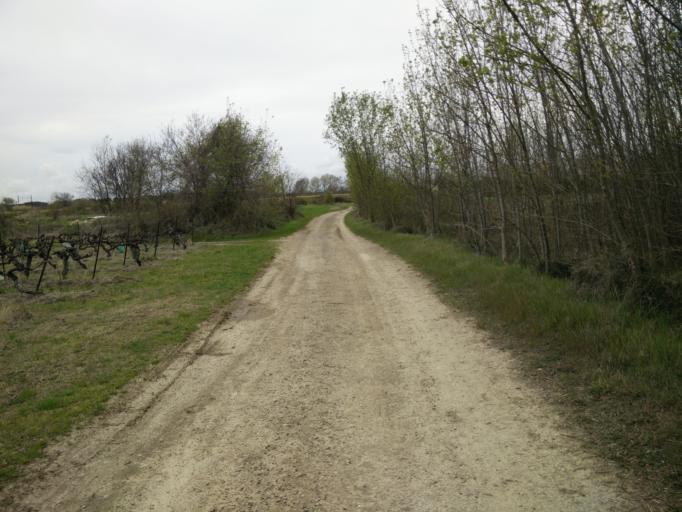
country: FR
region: Languedoc-Roussillon
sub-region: Departement du Gard
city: Gallargues-le-Montueux
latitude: 43.7109
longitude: 4.1688
